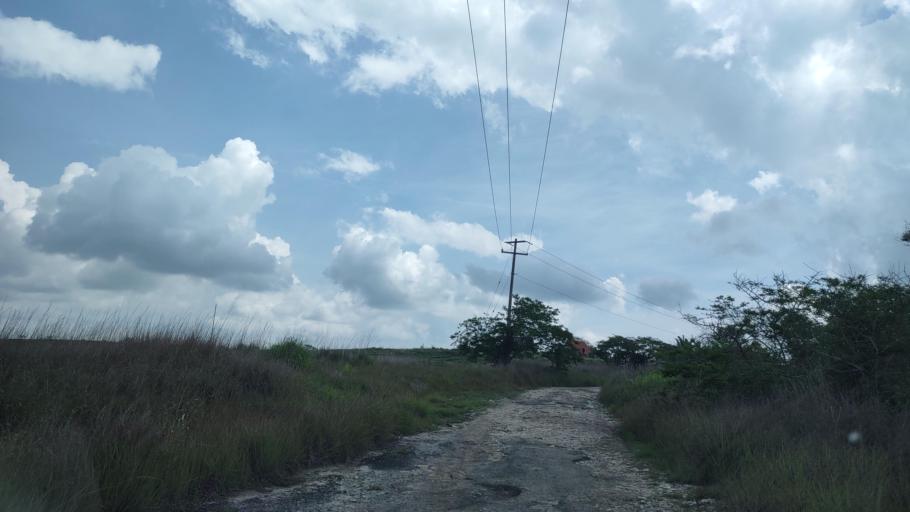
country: MX
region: Veracruz
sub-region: Emiliano Zapata
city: Dos Rios
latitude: 19.4577
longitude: -96.8080
